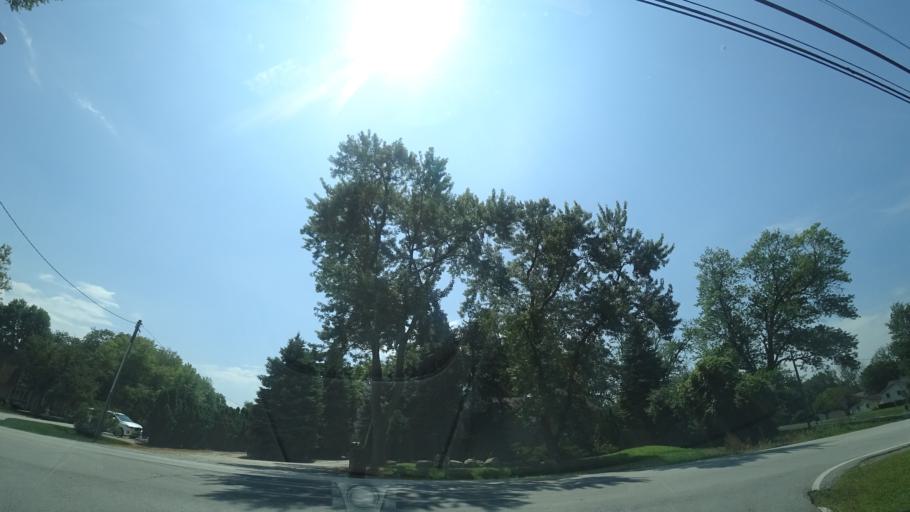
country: US
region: Illinois
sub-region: Cook County
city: Crestwood
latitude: 41.6615
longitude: -87.7606
